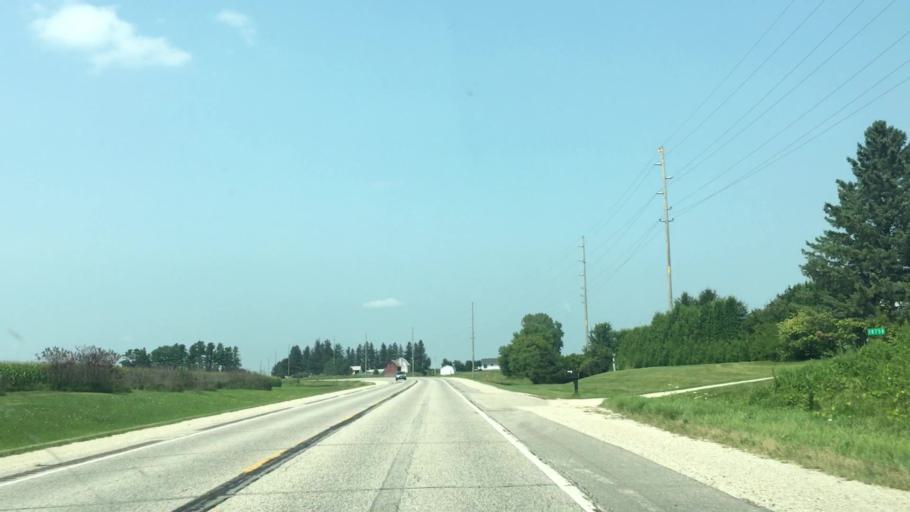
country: US
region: Iowa
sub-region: Fayette County
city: West Union
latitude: 42.9022
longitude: -91.8106
